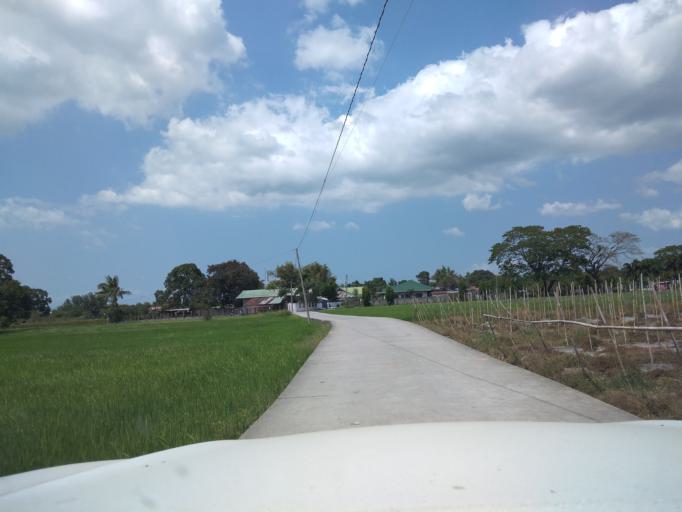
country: PH
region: Central Luzon
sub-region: Province of Pampanga
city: Bahay Pare
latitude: 15.0119
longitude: 120.8722
